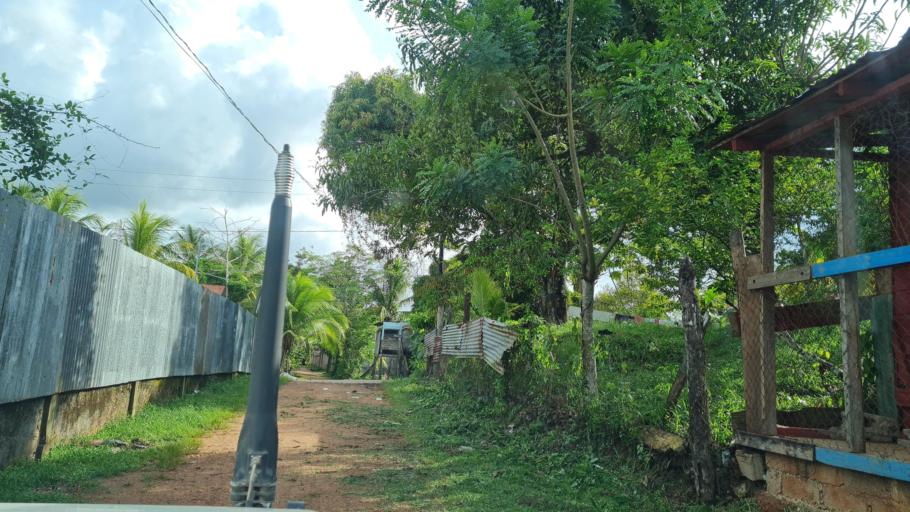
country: NI
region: Atlantico Norte (RAAN)
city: Waspam
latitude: 14.7448
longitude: -83.9702
